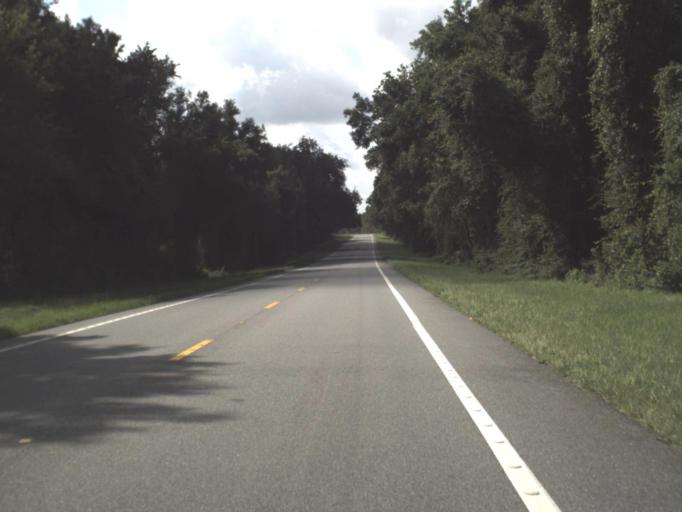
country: US
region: Florida
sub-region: Citrus County
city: Hernando
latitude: 28.9190
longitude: -82.3874
